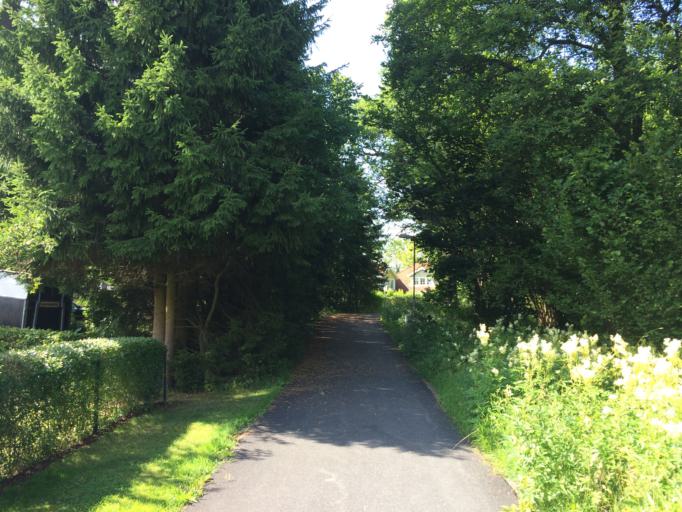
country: SE
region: Stockholm
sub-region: Sollentuna Kommun
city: Sollentuna
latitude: 59.4589
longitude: 17.9051
